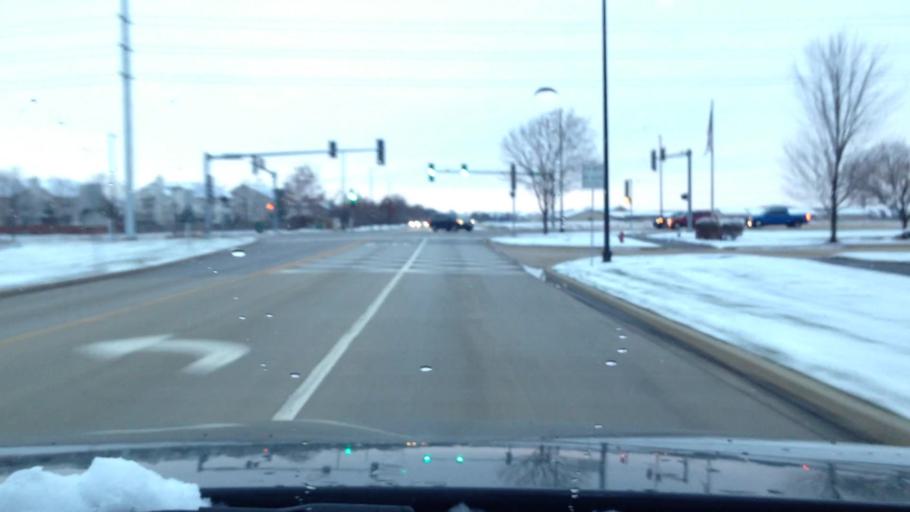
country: US
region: Illinois
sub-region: McHenry County
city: Huntley
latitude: 42.1829
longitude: -88.4020
